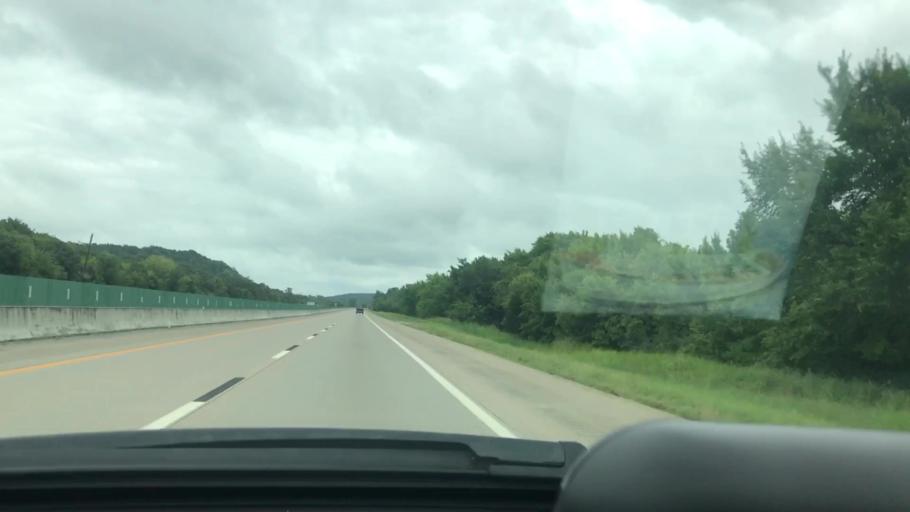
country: US
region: Oklahoma
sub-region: Pittsburg County
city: Krebs
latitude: 35.0852
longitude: -95.7015
